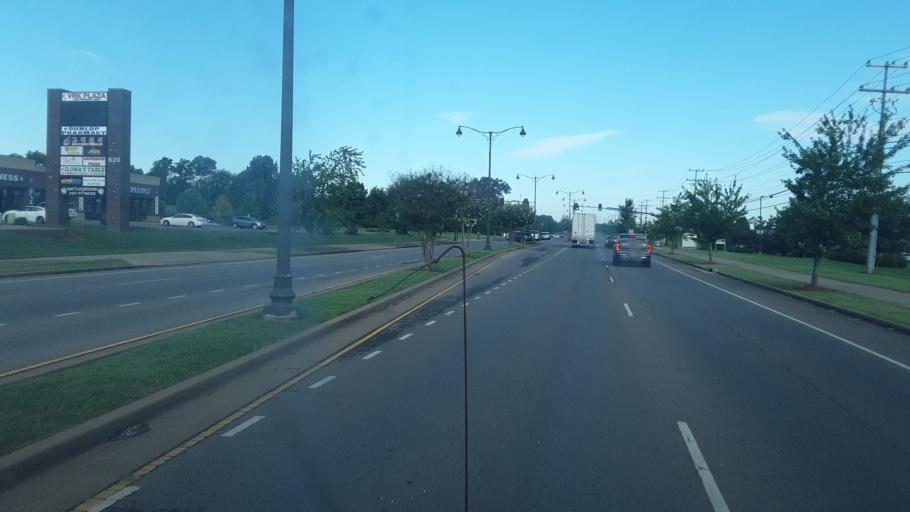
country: US
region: Tennessee
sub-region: Montgomery County
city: Clarksville
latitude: 36.5800
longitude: -87.2704
